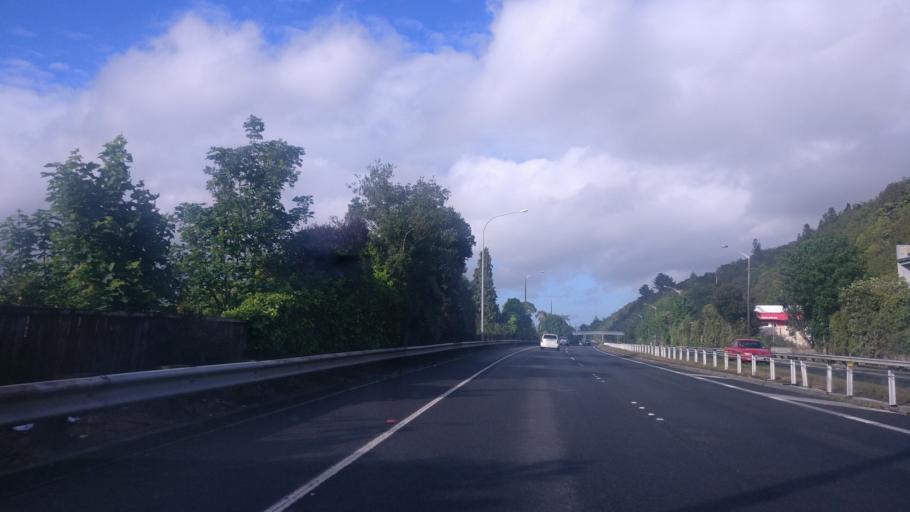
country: NZ
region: Wellington
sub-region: Lower Hutt City
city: Lower Hutt
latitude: -41.1839
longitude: 174.9404
